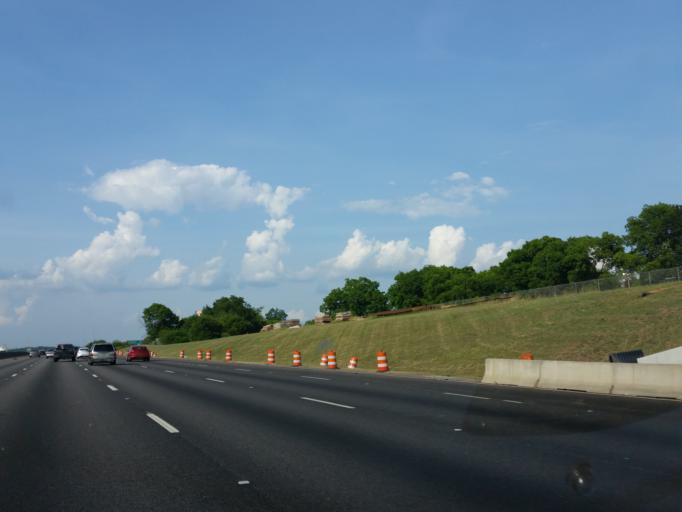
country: US
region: Alabama
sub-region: Jefferson County
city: Birmingham
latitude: 33.5359
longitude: -86.7952
